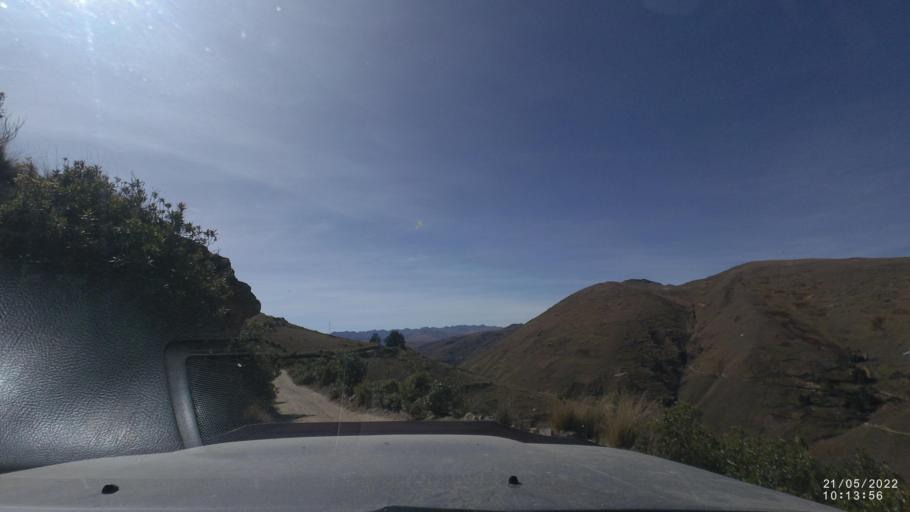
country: BO
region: Cochabamba
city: Colomi
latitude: -17.3333
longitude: -65.9732
